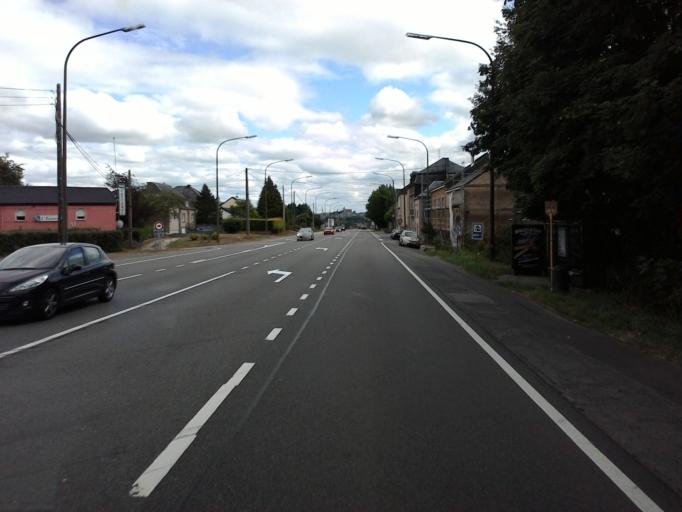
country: BE
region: Wallonia
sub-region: Province du Luxembourg
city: Arlon
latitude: 49.7075
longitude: 5.8041
